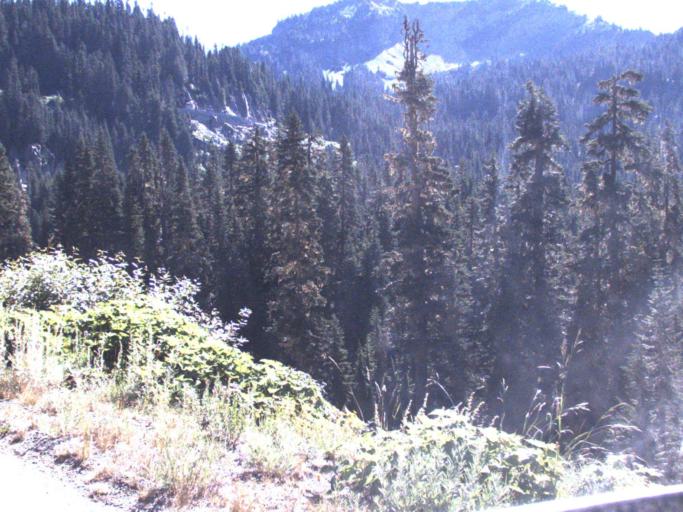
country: US
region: Washington
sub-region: King County
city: Enumclaw
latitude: 46.8669
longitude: -121.5354
